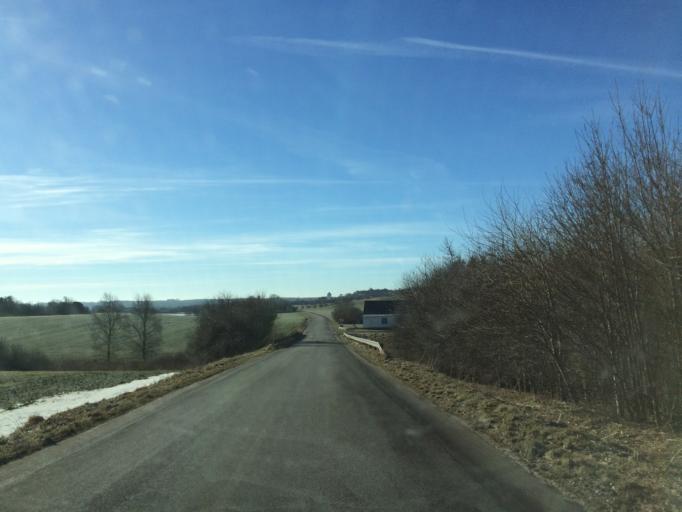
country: DK
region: North Denmark
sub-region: Vesthimmerland Kommune
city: Alestrup
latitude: 56.6011
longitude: 9.6298
